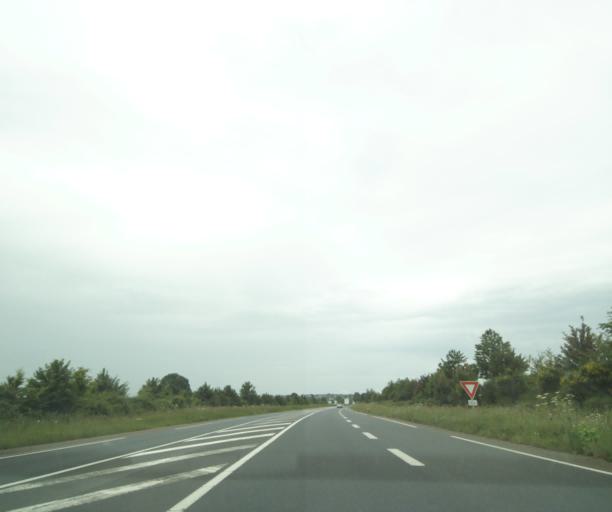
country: FR
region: Poitou-Charentes
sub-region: Departement des Deux-Sevres
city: Saint-Pardoux
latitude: 46.5485
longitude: -0.3117
